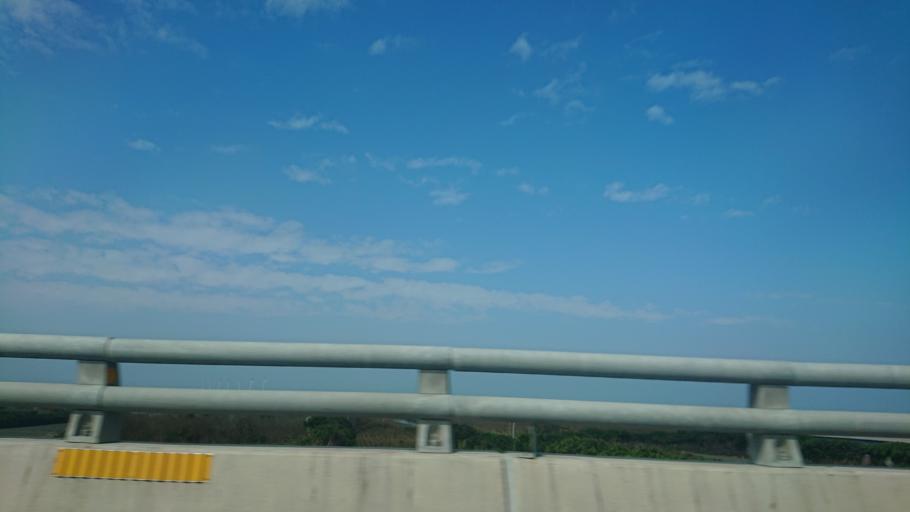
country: TW
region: Taiwan
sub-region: Changhua
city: Chang-hua
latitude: 23.9843
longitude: 120.3666
